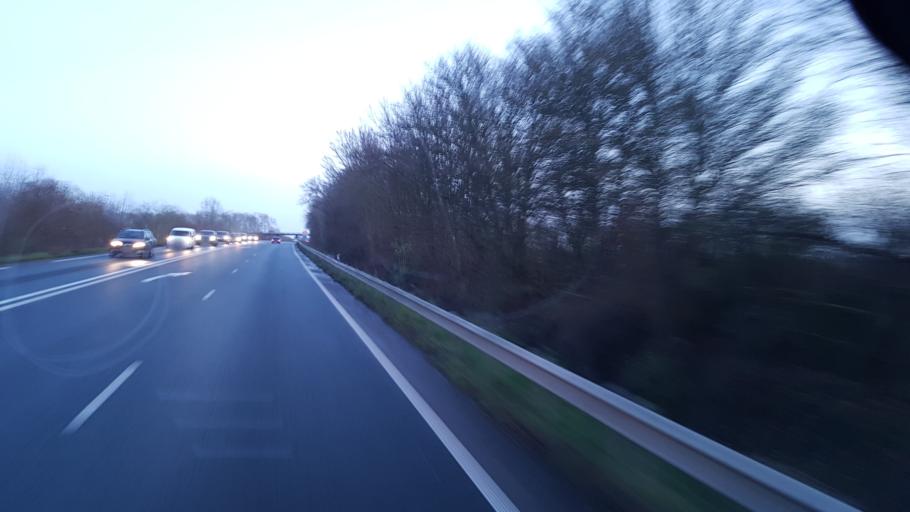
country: FR
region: Nord-Pas-de-Calais
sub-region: Departement du Nord
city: Lambres-lez-Douai
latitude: 50.3451
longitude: 3.0732
